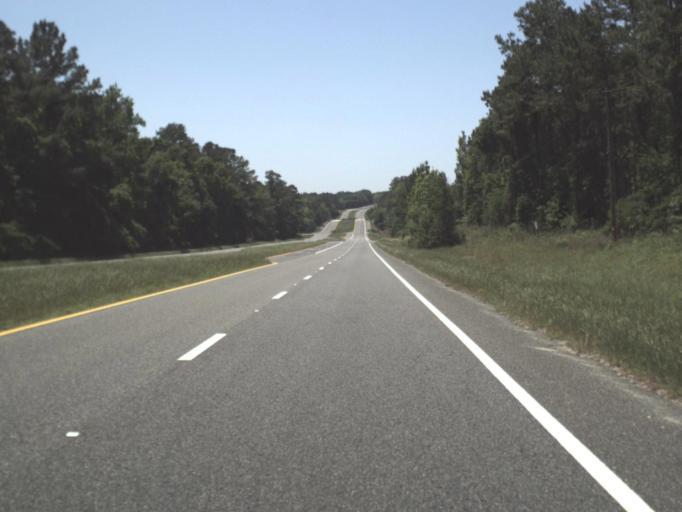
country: US
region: Florida
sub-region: Jefferson County
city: Monticello
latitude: 30.5037
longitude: -83.8785
